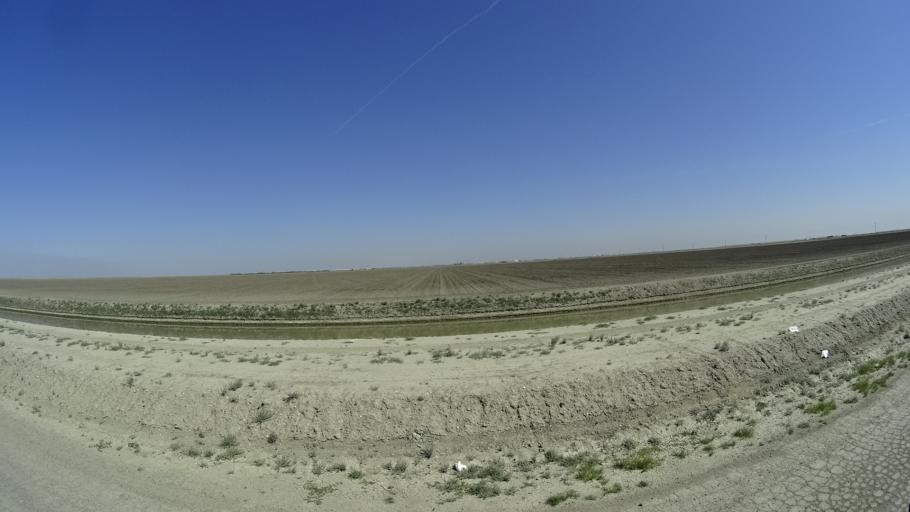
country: US
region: California
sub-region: Tulare County
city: Alpaugh
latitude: 35.9780
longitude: -119.5400
